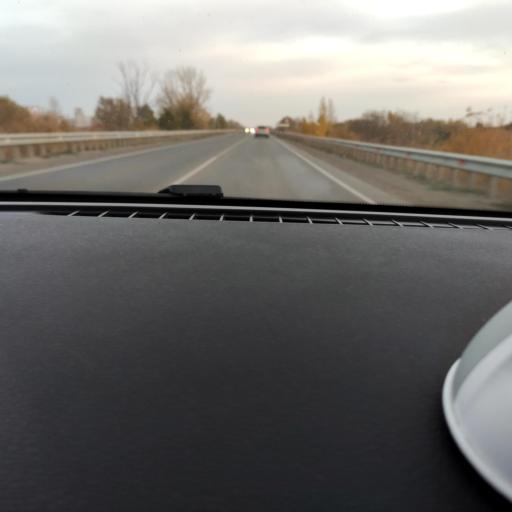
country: RU
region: Samara
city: Samara
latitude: 53.1032
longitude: 50.1387
